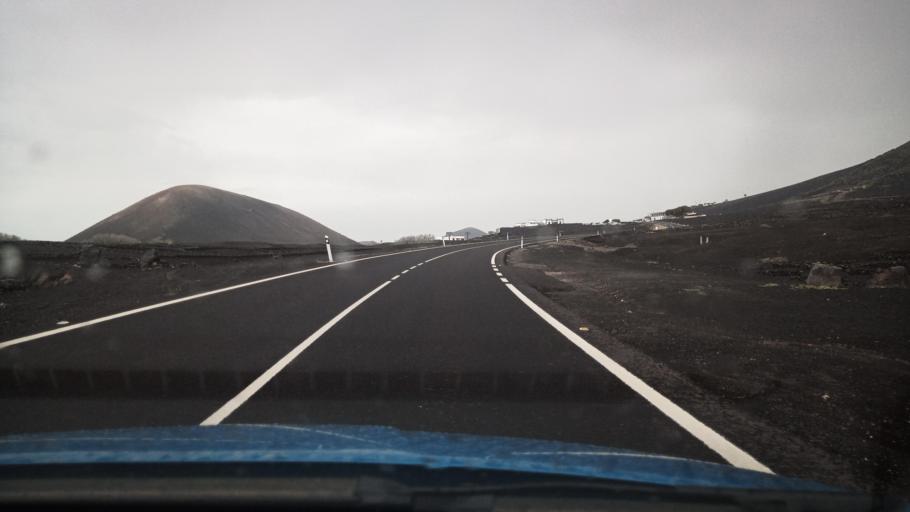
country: ES
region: Canary Islands
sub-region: Provincia de Las Palmas
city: Yaiza
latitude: 28.9663
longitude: -13.7205
